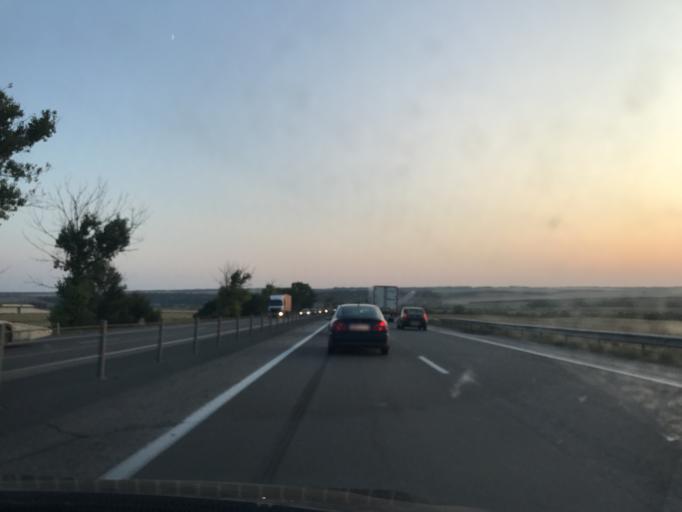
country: RU
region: Rostov
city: Mayskiy
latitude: 47.6577
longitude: 40.0420
